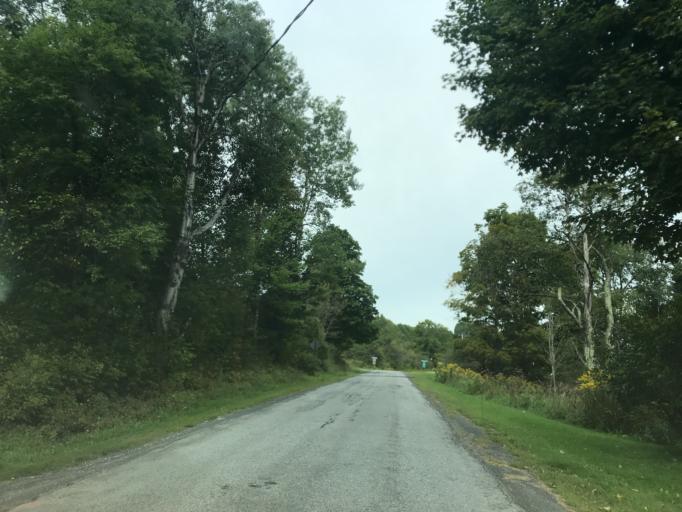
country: US
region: New York
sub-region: Otsego County
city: Worcester
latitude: 42.5661
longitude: -74.6697
